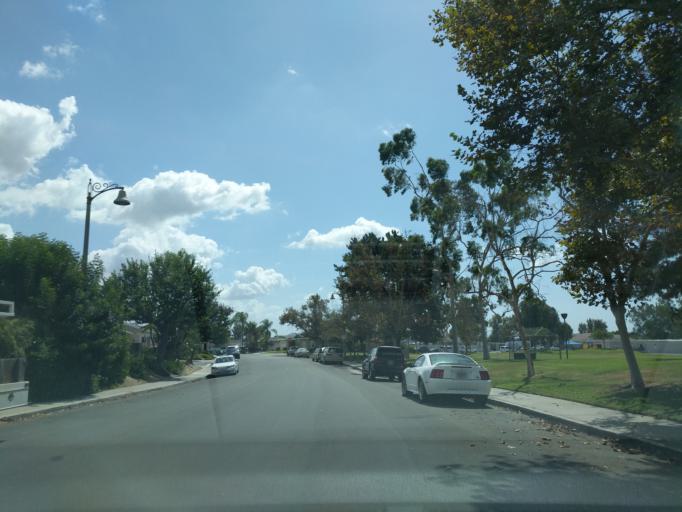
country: US
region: California
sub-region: Orange County
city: Ladera Ranch
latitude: 33.5721
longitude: -117.6554
